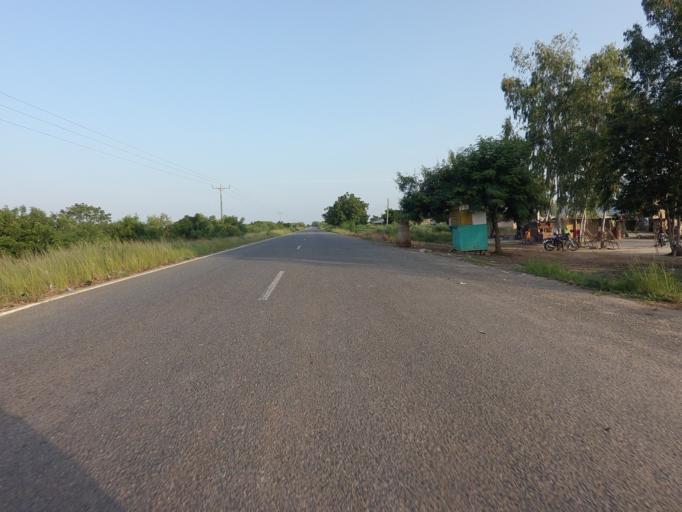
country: GH
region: Volta
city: Anloga
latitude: 5.9044
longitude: 0.7117
